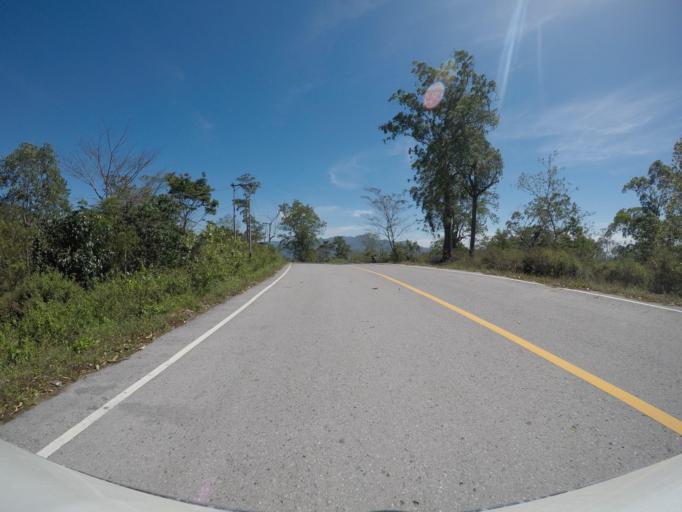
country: TL
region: Manufahi
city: Same
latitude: -8.8922
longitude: 125.9831
